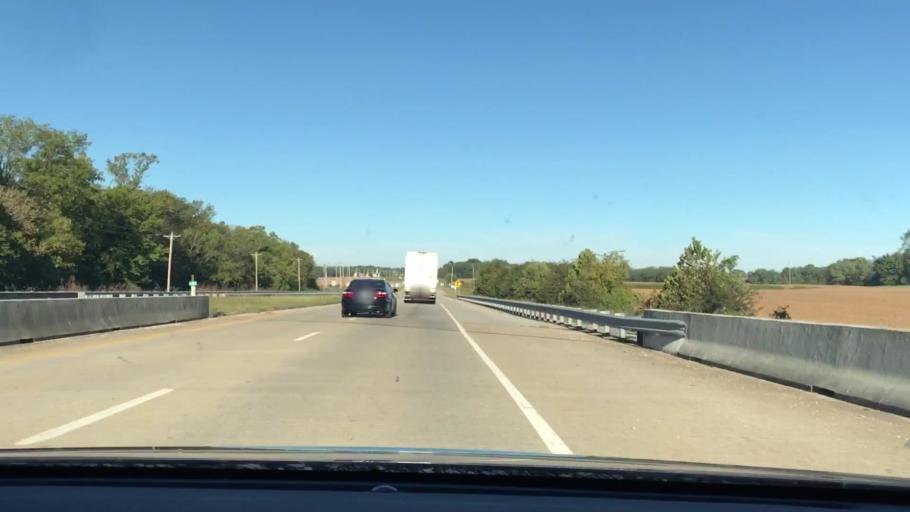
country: US
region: Kentucky
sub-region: Christian County
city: Hopkinsville
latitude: 36.8326
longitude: -87.5251
